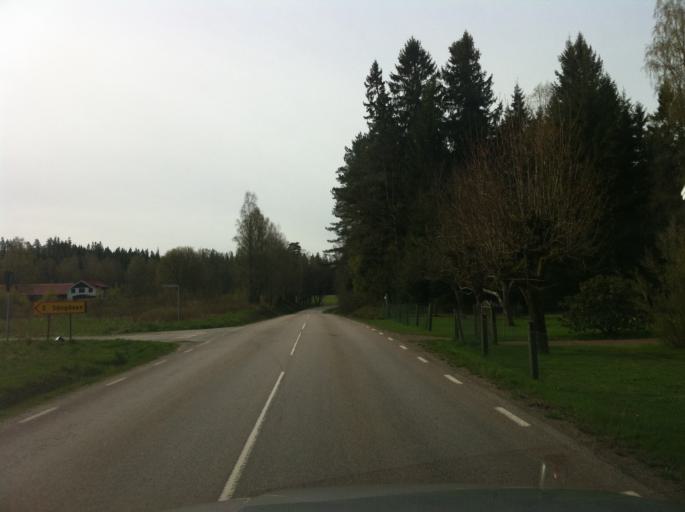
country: SE
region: Vaestra Goetaland
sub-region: Bollebygds Kommun
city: Bollebygd
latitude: 57.7185
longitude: 12.5857
